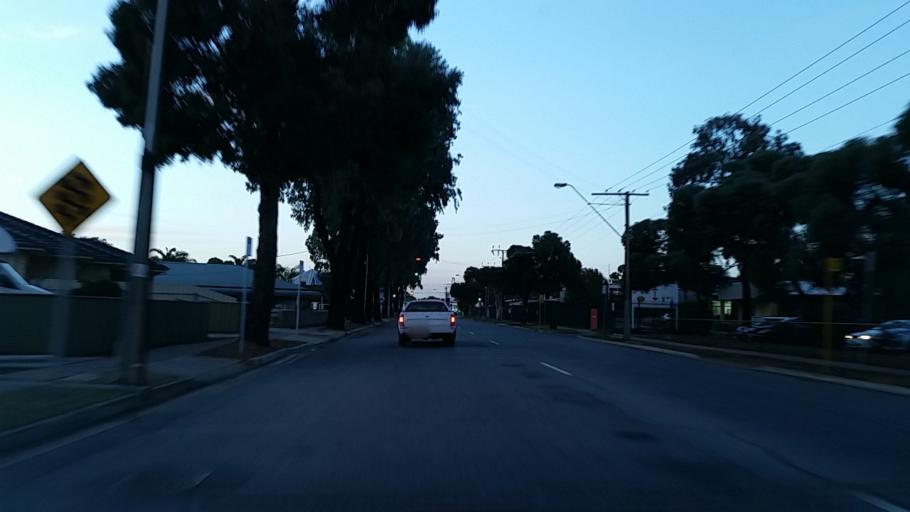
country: AU
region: South Australia
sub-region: Salisbury
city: Salisbury
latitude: -34.7643
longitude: 138.6495
